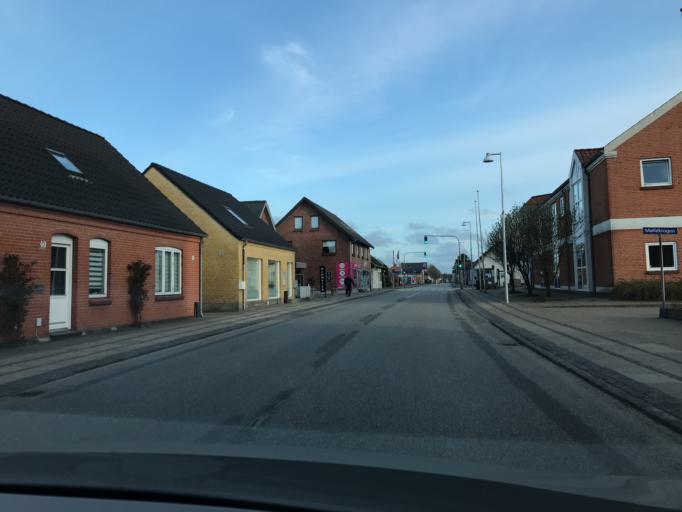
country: DK
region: Central Jutland
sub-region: Herning Kommune
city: Sunds
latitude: 56.2037
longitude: 9.0166
